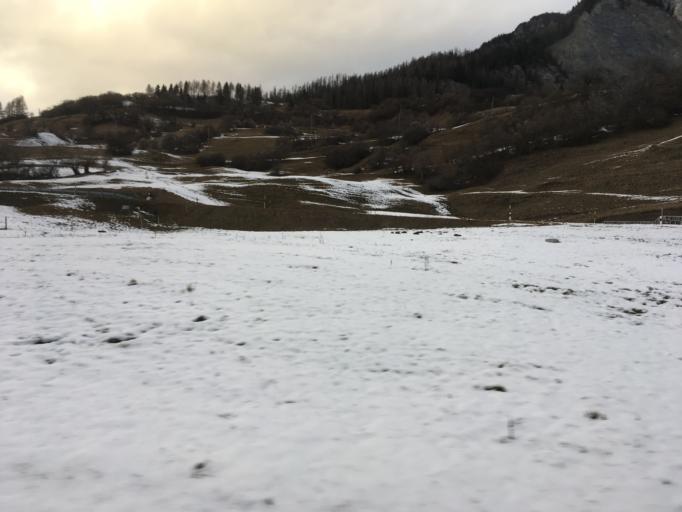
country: CH
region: Grisons
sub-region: Albula District
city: Tiefencastel
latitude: 46.6650
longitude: 9.5900
